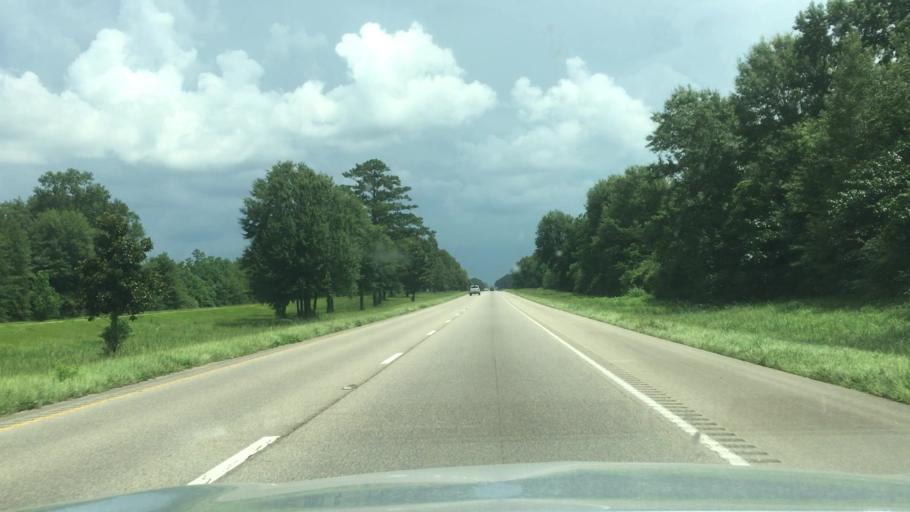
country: US
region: Mississippi
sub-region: Pearl River County
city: Picayune
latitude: 30.5555
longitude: -89.6427
